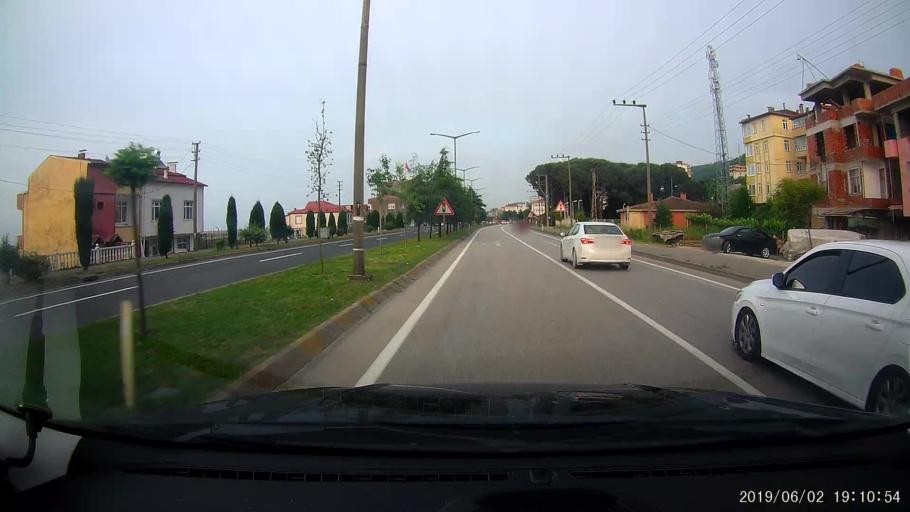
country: TR
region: Ordu
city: Gulyali
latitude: 40.9674
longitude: 38.0535
